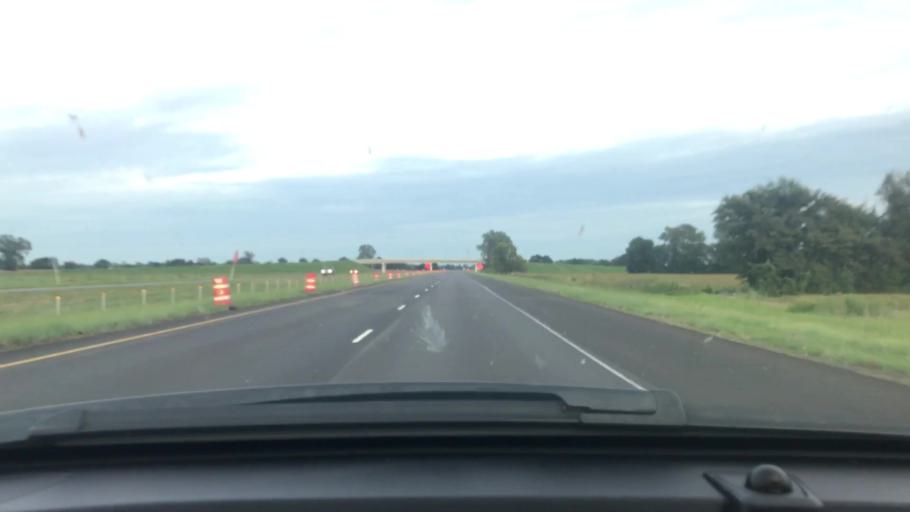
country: US
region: Arkansas
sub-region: Poinsett County
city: Trumann
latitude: 35.6489
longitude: -90.5232
